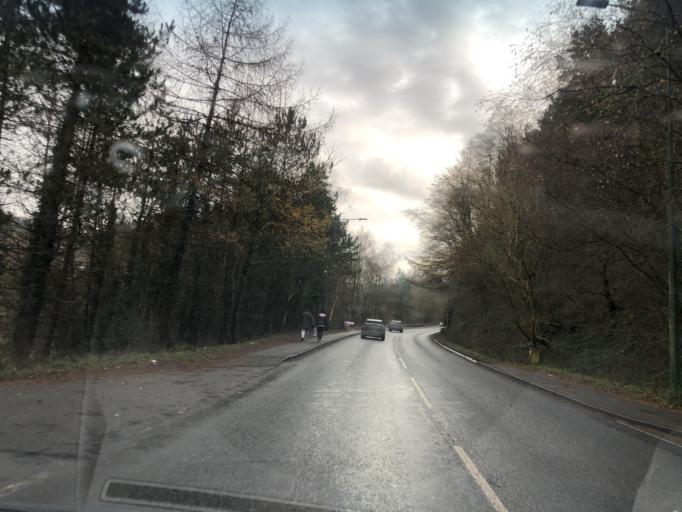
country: GB
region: Wales
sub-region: Blaenau Gwent
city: Abertillery
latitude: 51.7271
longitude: -3.1357
